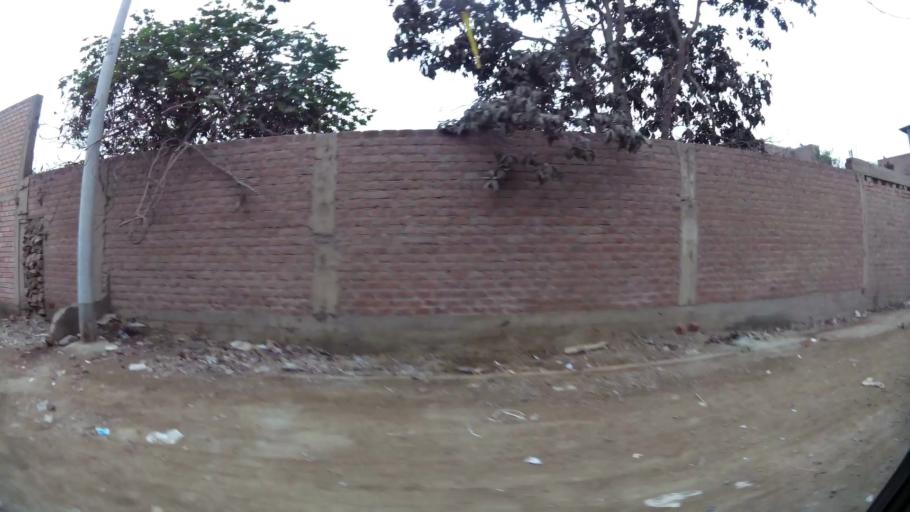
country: PE
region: Lima
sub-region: Lima
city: Urb. Santo Domingo
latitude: -11.8991
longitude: -77.0635
